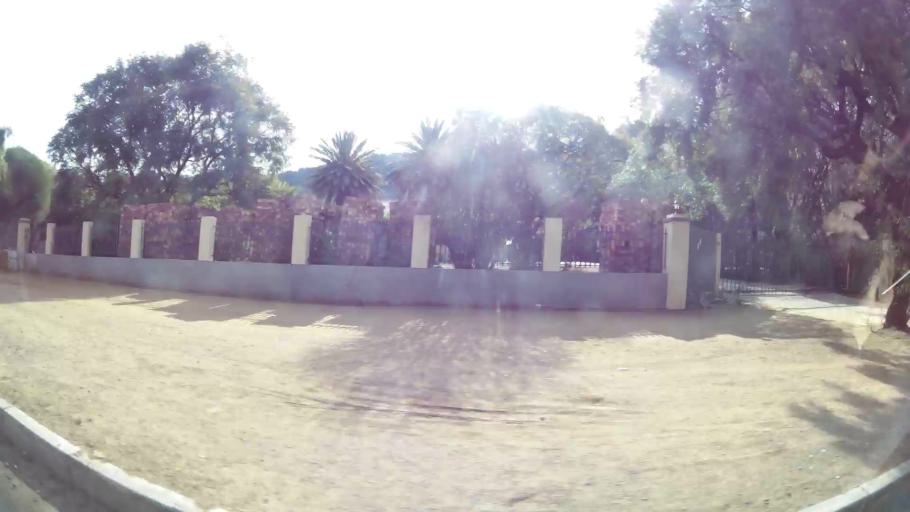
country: ZA
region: Orange Free State
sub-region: Mangaung Metropolitan Municipality
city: Bloemfontein
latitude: -29.1070
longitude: 26.2352
